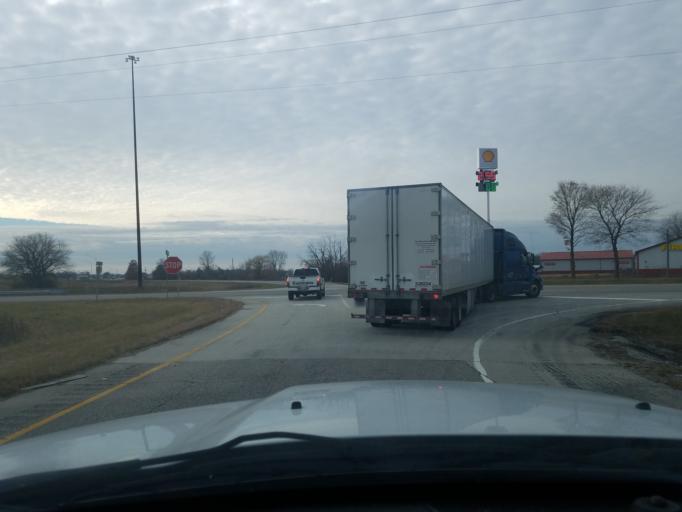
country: US
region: Indiana
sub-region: Huntington County
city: Warren
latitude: 40.7211
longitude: -85.4366
